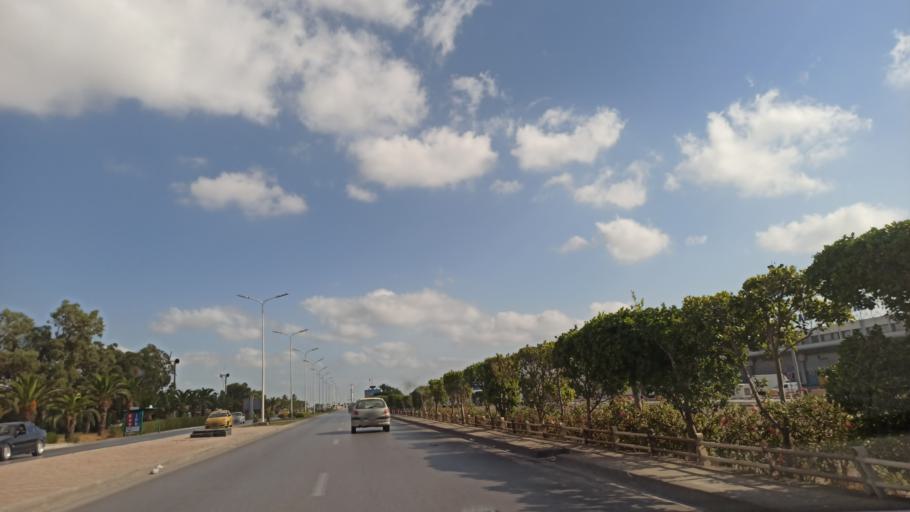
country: TN
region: Ariana
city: Ariana
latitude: 36.8360
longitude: 10.2131
